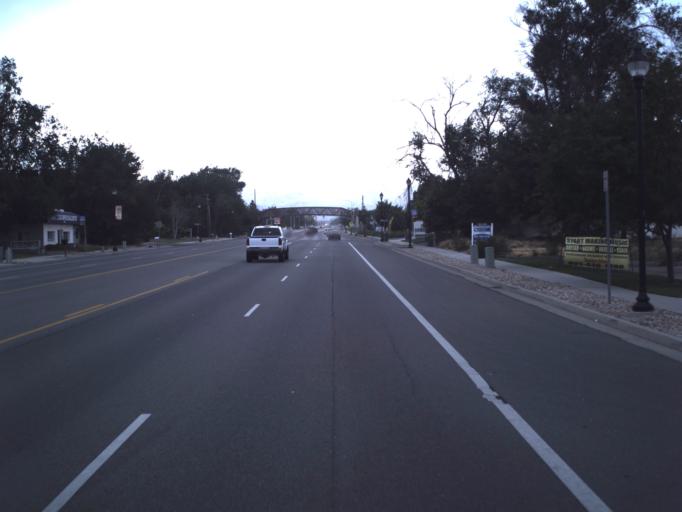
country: US
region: Utah
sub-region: Salt Lake County
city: Riverton
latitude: 40.5224
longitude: -111.9528
